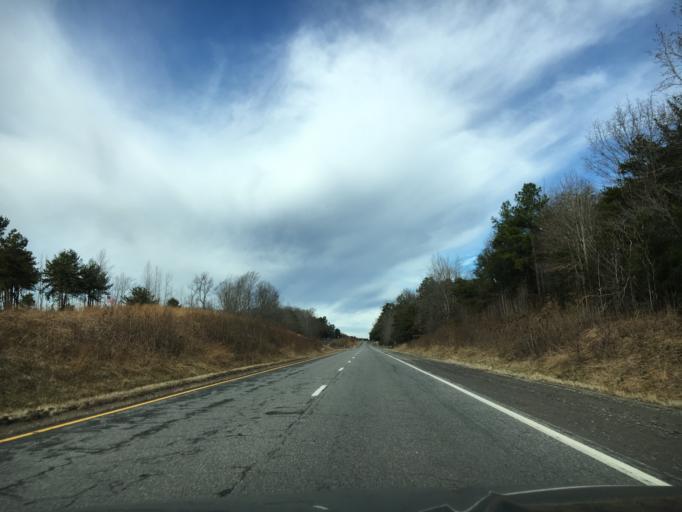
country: US
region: Virginia
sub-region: Nottoway County
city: Crewe
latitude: 37.2190
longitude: -78.2336
